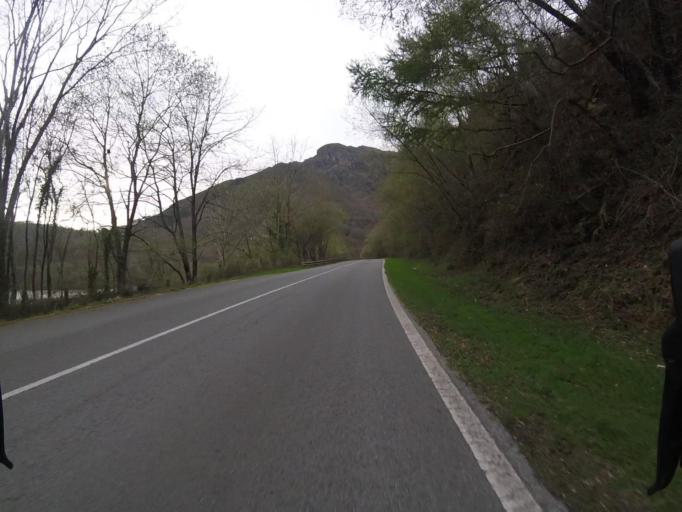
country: ES
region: Basque Country
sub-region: Provincia de Guipuzcoa
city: Irun
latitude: 43.2758
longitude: -1.7704
